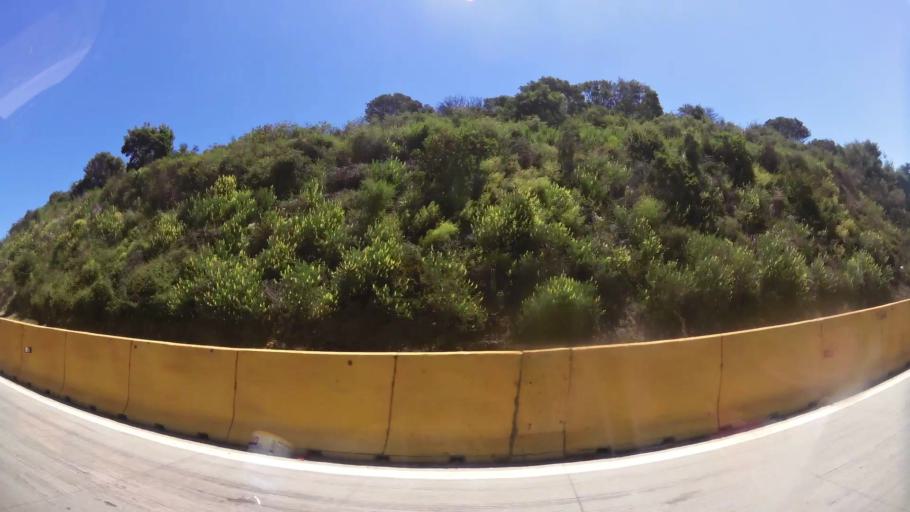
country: CL
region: Valparaiso
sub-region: Provincia de Valparaiso
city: Valparaiso
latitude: -33.0623
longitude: -71.6415
